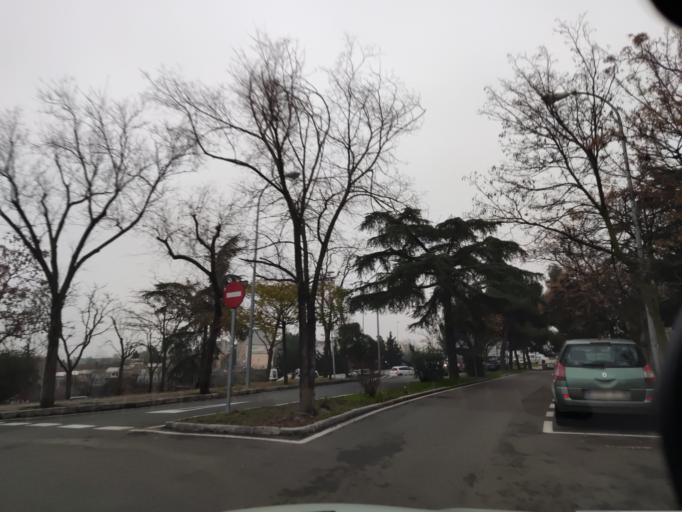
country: ES
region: Madrid
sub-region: Provincia de Madrid
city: Tetuan de las Victorias
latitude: 40.4907
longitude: -3.6999
